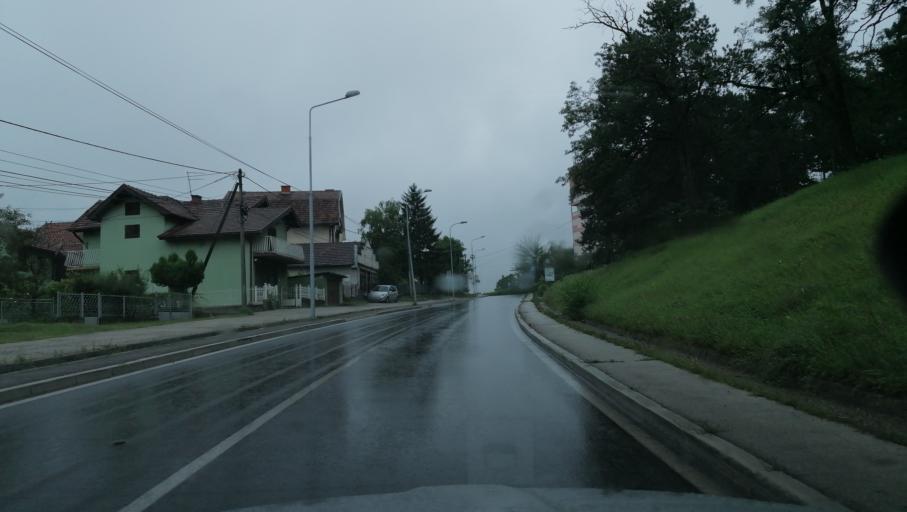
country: RS
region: Central Serbia
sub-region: Raski Okrug
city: Kraljevo
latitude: 43.7287
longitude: 20.6737
